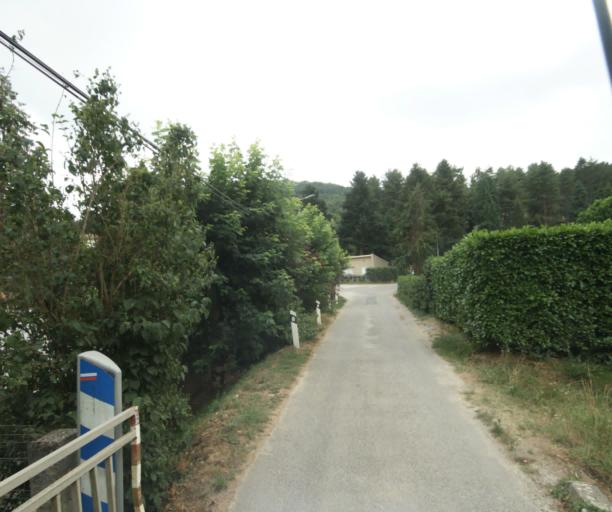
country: FR
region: Midi-Pyrenees
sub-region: Departement du Tarn
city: Soreze
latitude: 43.4343
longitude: 2.0408
